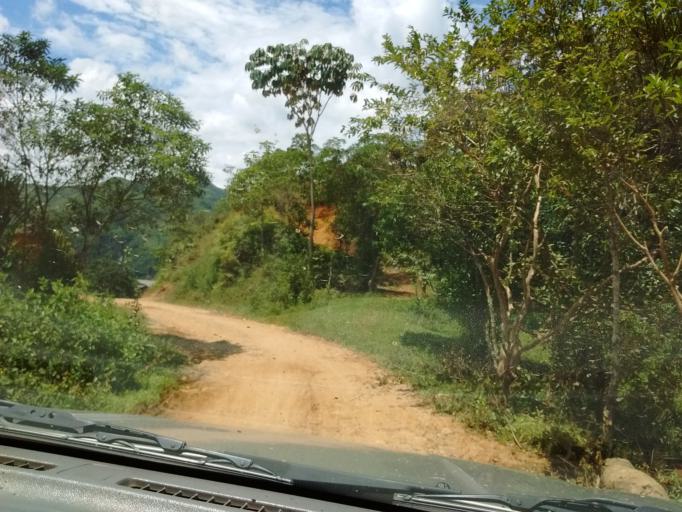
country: CO
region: Cauca
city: Villa Rica
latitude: 2.6399
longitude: -76.7698
